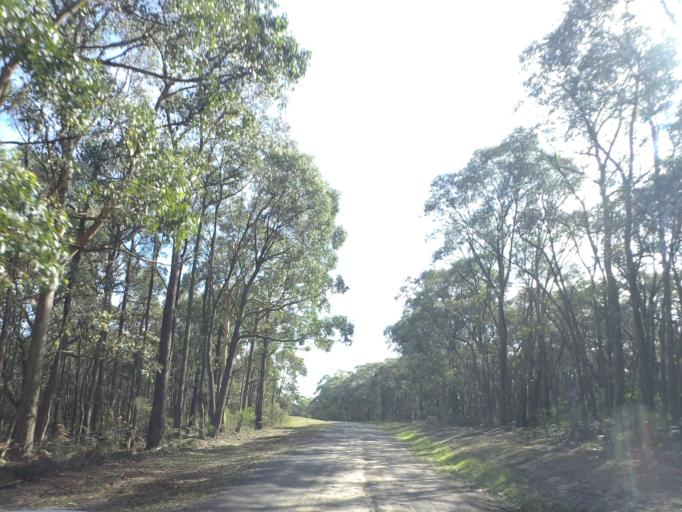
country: AU
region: Victoria
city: Brown Hill
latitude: -37.4403
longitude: 144.2059
